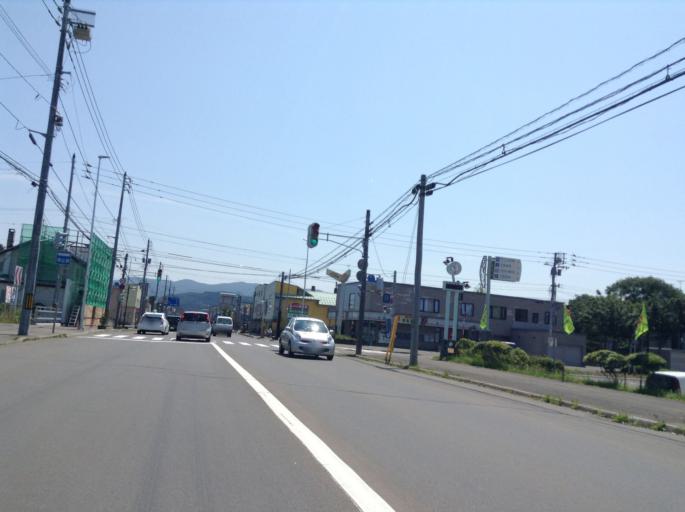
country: JP
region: Hokkaido
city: Nayoro
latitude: 44.3047
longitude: 142.6322
